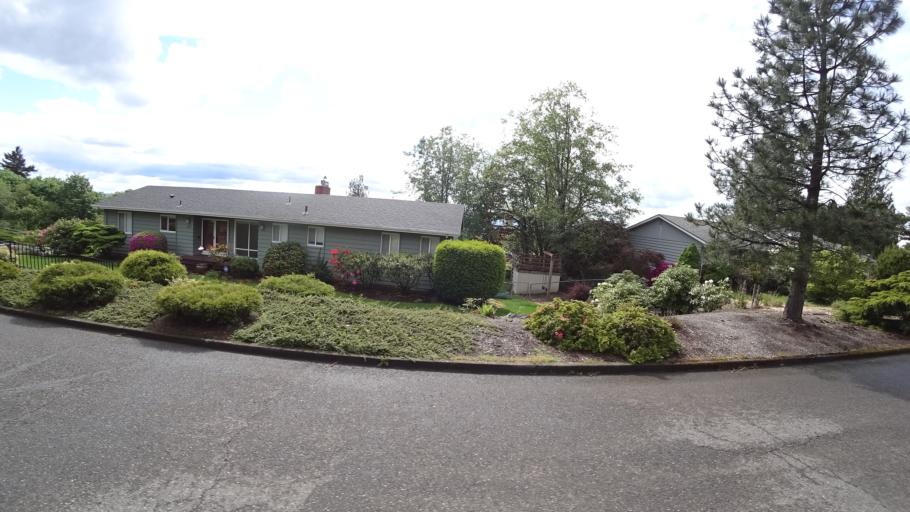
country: US
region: Oregon
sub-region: Washington County
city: West Haven
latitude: 45.5403
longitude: -122.7599
